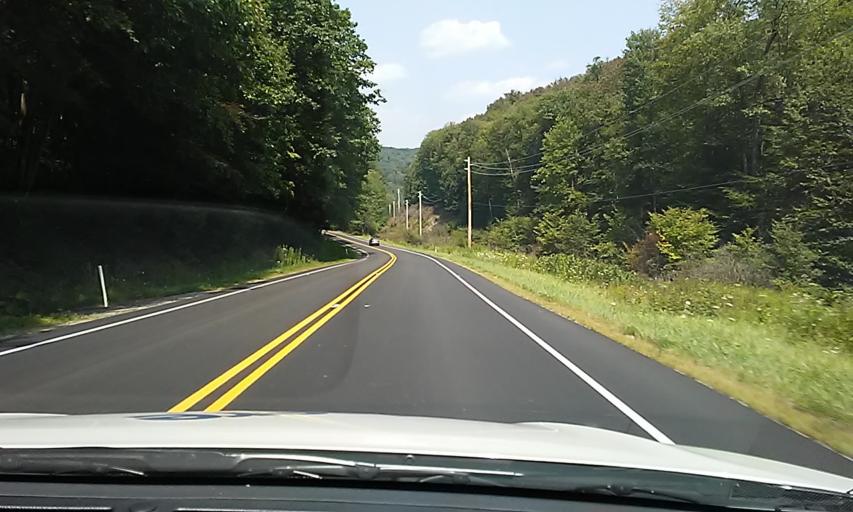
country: US
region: Pennsylvania
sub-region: Elk County
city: Saint Marys
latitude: 41.4604
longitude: -78.4286
